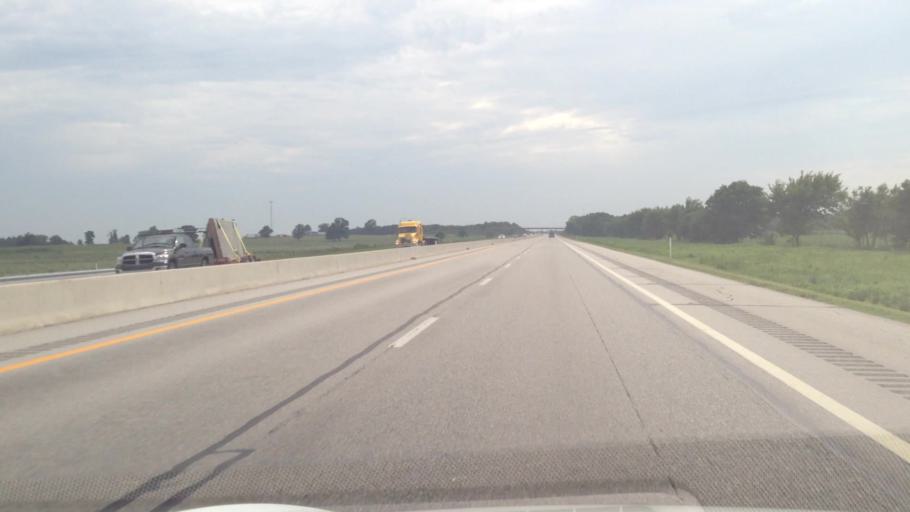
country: US
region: Kansas
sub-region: Cherokee County
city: Baxter Springs
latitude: 36.9546
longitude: -94.6709
